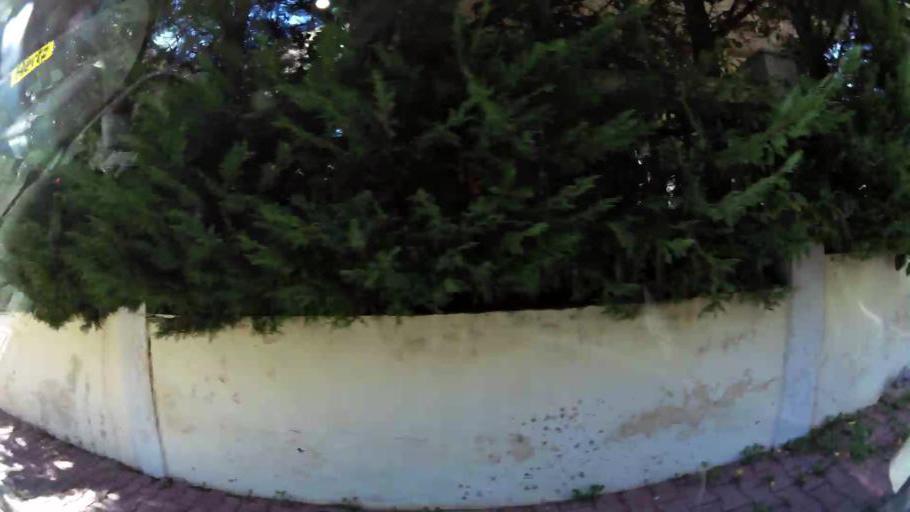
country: GR
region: Attica
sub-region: Nomarchia Athinas
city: Vrilissia
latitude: 38.0365
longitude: 23.8429
